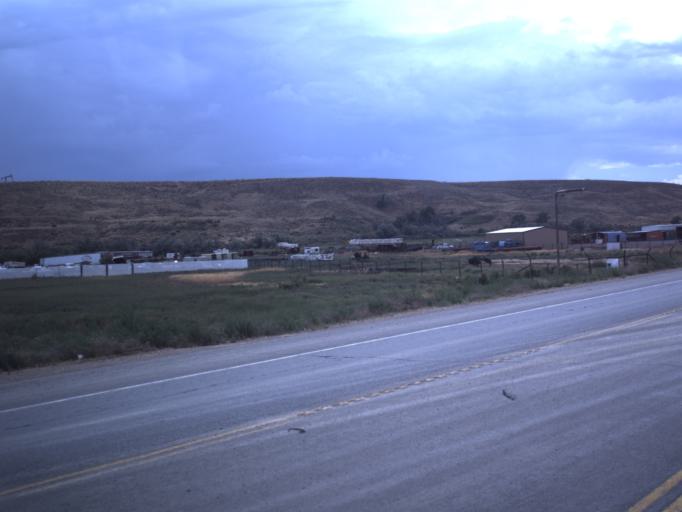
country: US
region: Utah
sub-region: Duchesne County
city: Roosevelt
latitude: 40.2616
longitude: -110.0538
